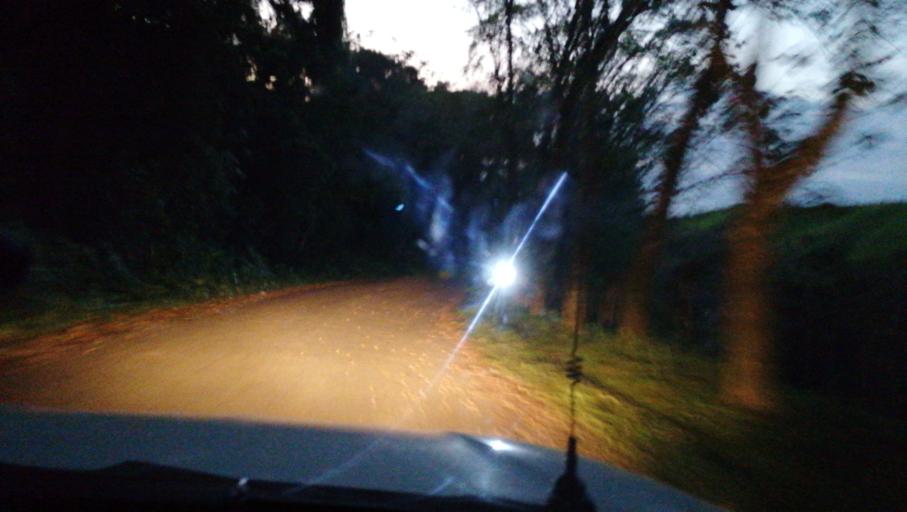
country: MX
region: Chiapas
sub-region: Ostuacan
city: Nuevo Juan del Grijalva
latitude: 17.4800
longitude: -93.3479
